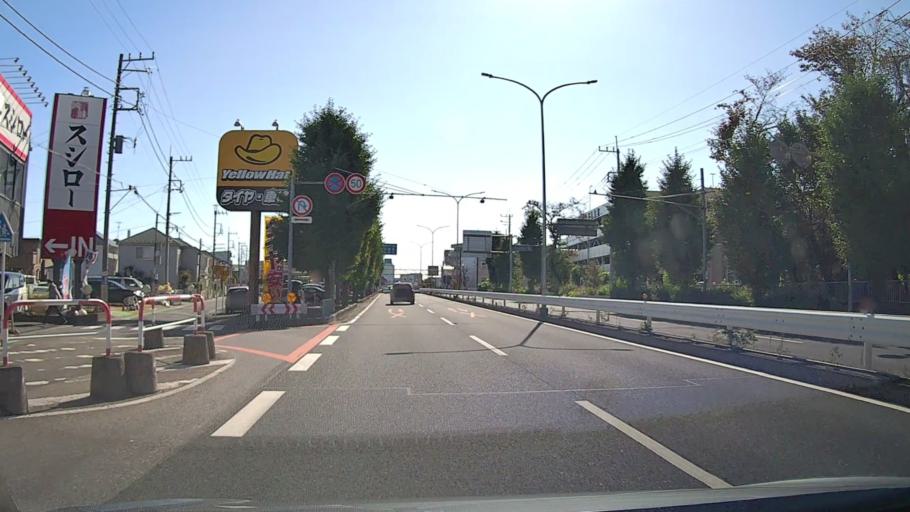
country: JP
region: Saitama
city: Wako
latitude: 35.7762
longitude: 139.6198
